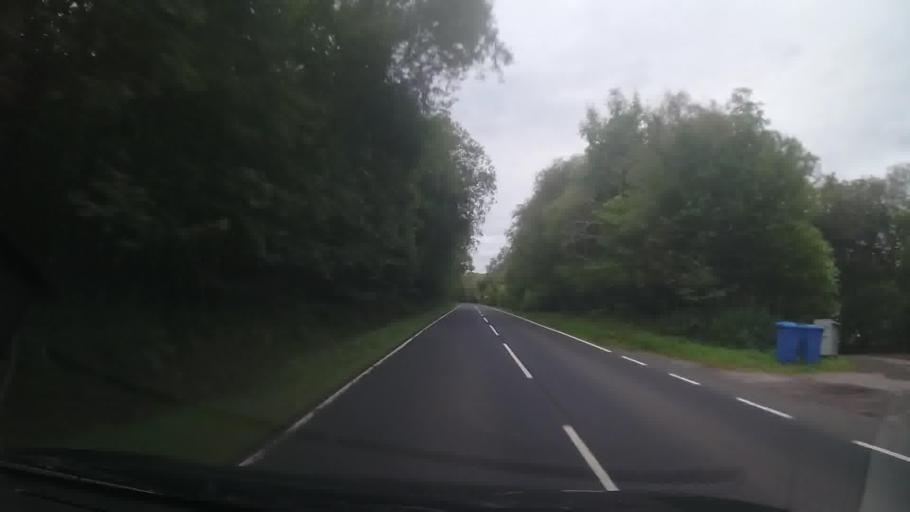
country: GB
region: Scotland
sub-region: Argyll and Bute
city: Garelochhead
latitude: 56.2107
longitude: -5.0544
